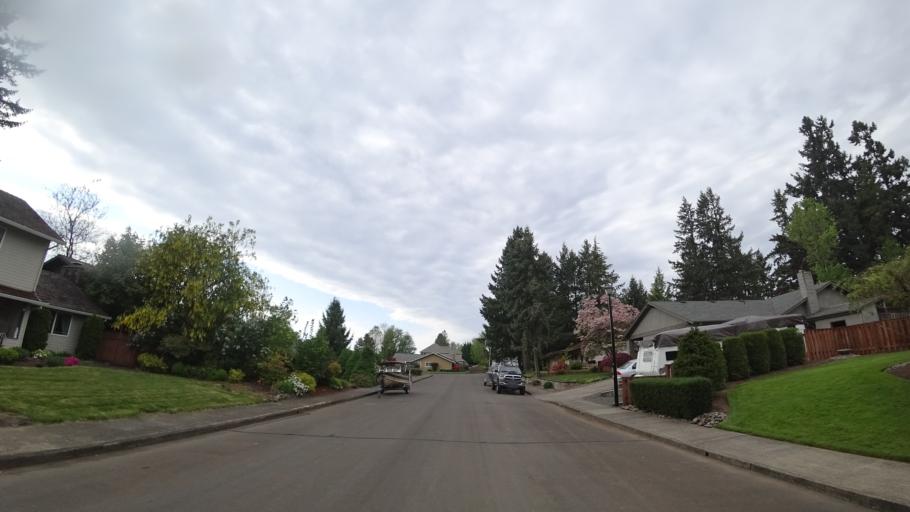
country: US
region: Oregon
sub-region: Washington County
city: Hillsboro
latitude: 45.4919
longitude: -122.9554
